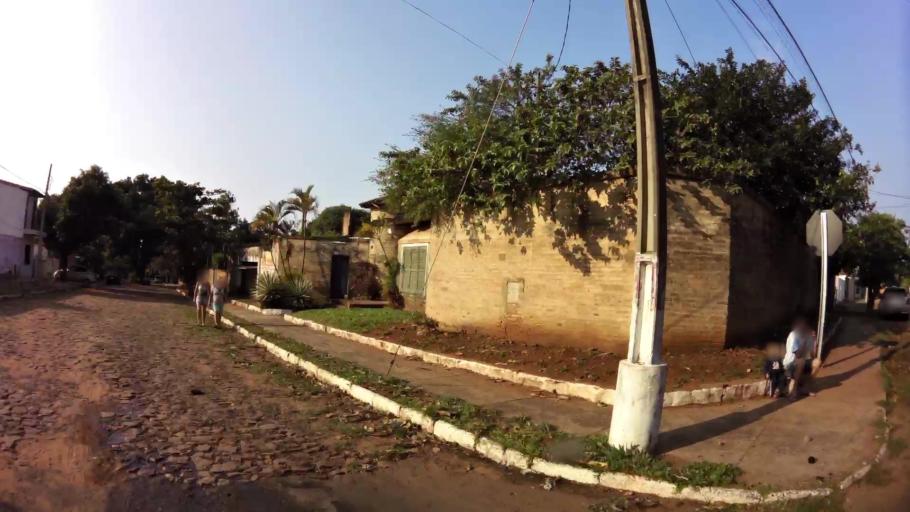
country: PY
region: Central
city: Lambare
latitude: -25.3434
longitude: -57.5956
